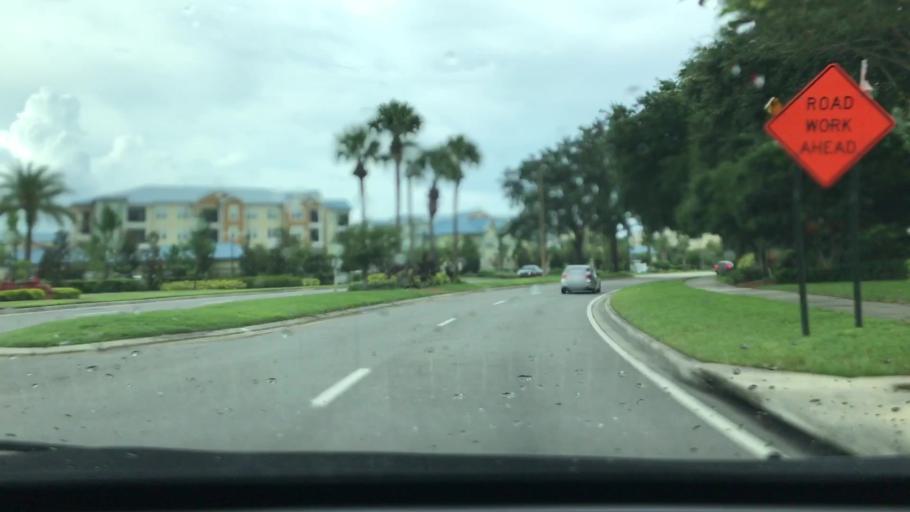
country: US
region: Florida
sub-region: Orange County
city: Williamsburg
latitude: 28.4064
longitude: -81.4743
